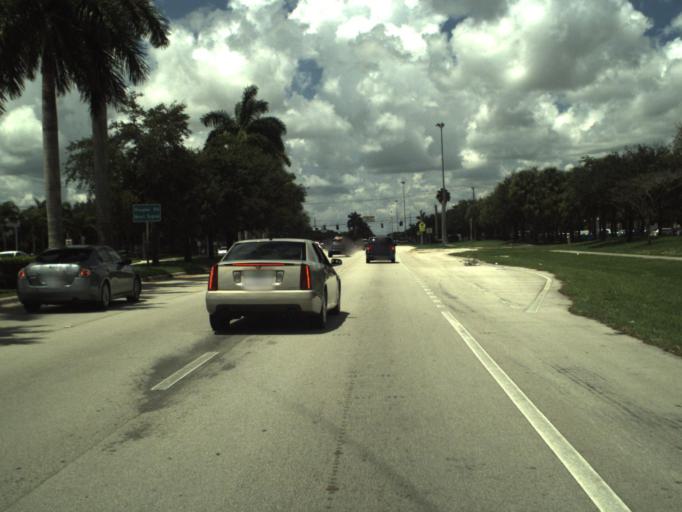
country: US
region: Florida
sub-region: Broward County
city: Miramar
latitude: 26.0089
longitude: -80.2609
